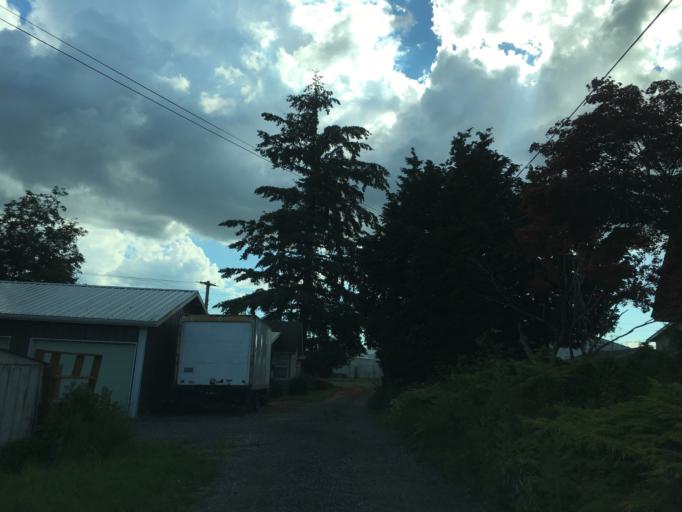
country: US
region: Washington
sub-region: Whatcom County
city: Lynden
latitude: 48.9468
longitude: -122.4454
